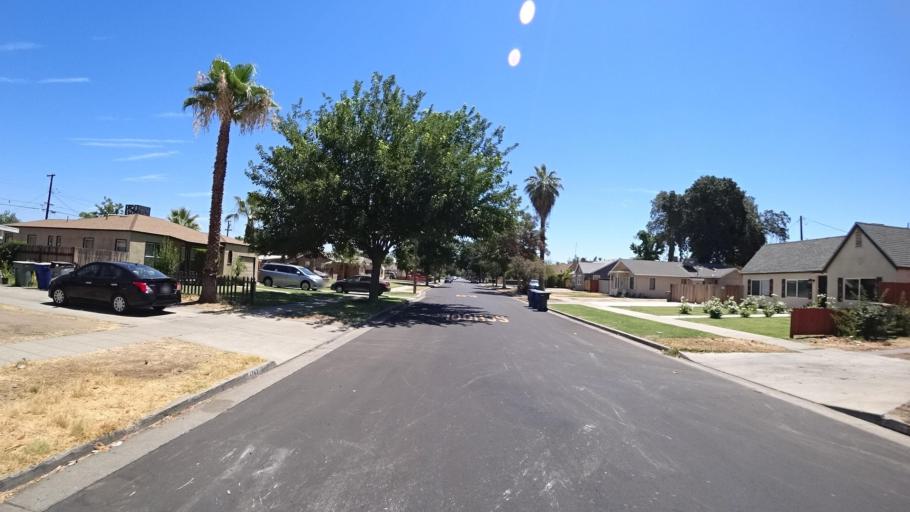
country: US
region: California
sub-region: Fresno County
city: Fresno
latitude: 36.7450
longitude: -119.7380
